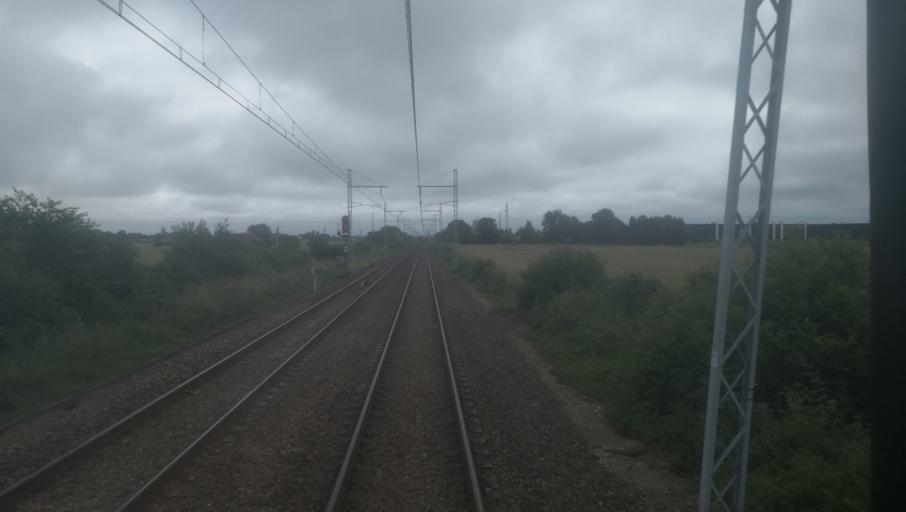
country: FR
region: Centre
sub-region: Departement de l'Indre
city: Saint-Maur
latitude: 46.7839
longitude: 1.6450
